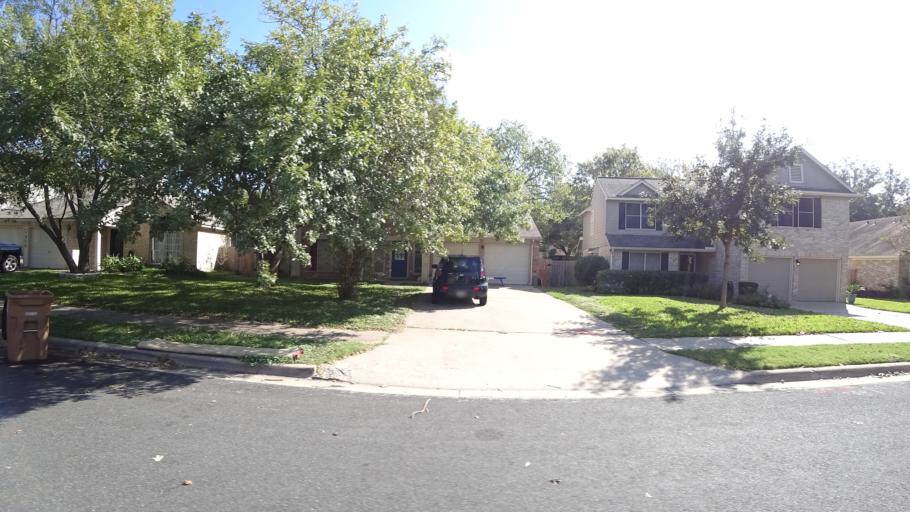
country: US
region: Texas
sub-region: Travis County
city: Shady Hollow
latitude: 30.1986
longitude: -97.8239
